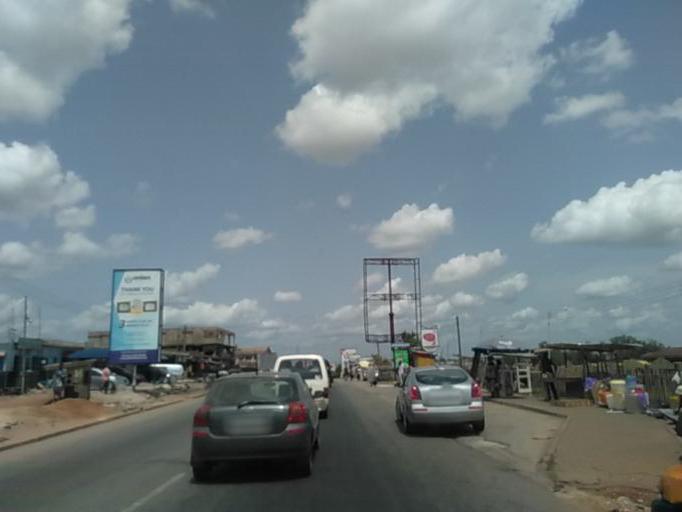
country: GH
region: Ashanti
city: Kumasi
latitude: 6.6627
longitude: -1.6013
